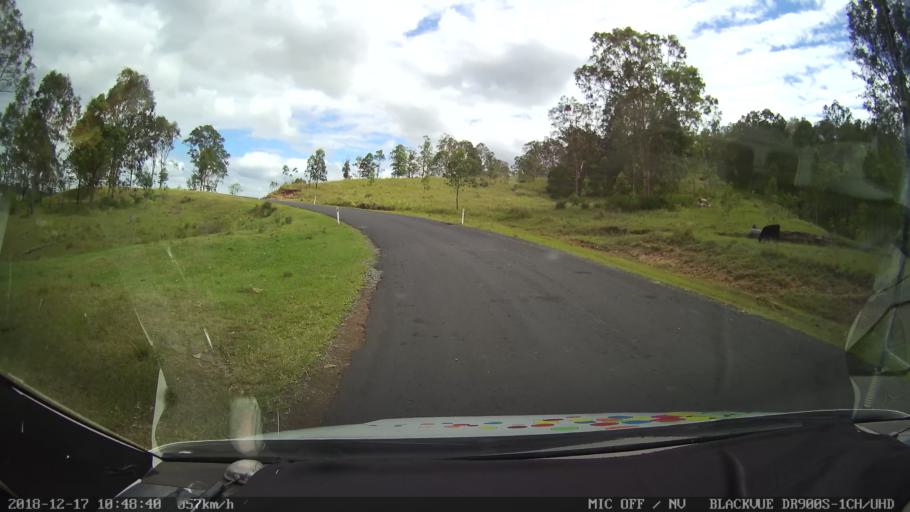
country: AU
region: New South Wales
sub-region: Clarence Valley
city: Gordon
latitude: -28.8711
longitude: 152.5716
